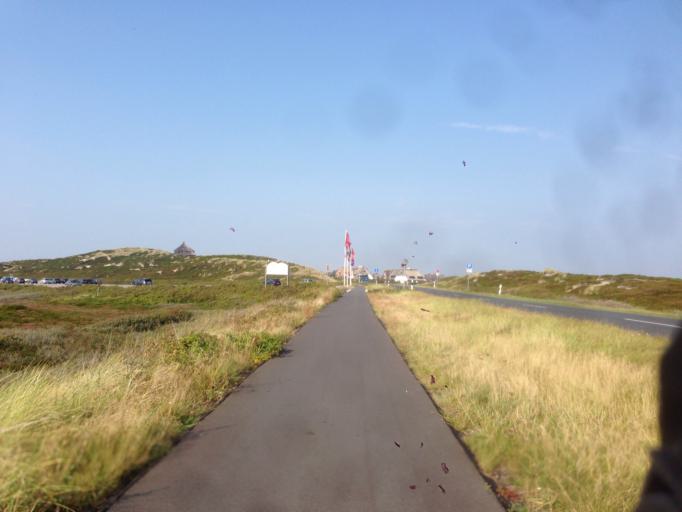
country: DE
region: Schleswig-Holstein
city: Westerland
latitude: 54.8378
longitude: 8.2920
